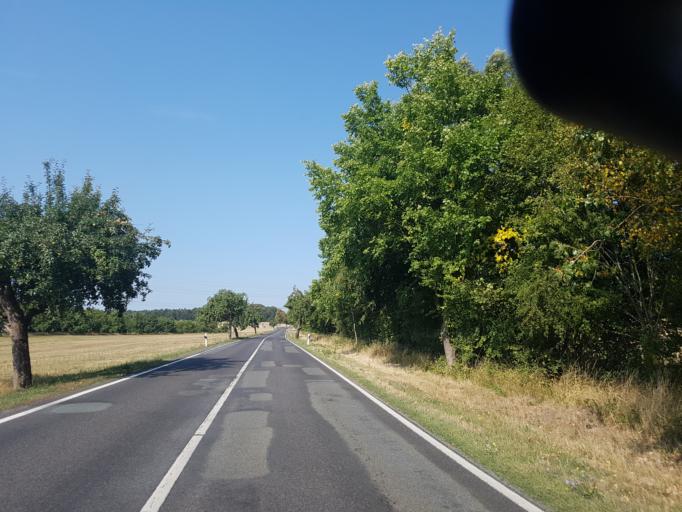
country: DE
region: Brandenburg
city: Belzig
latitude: 52.1311
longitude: 12.5389
